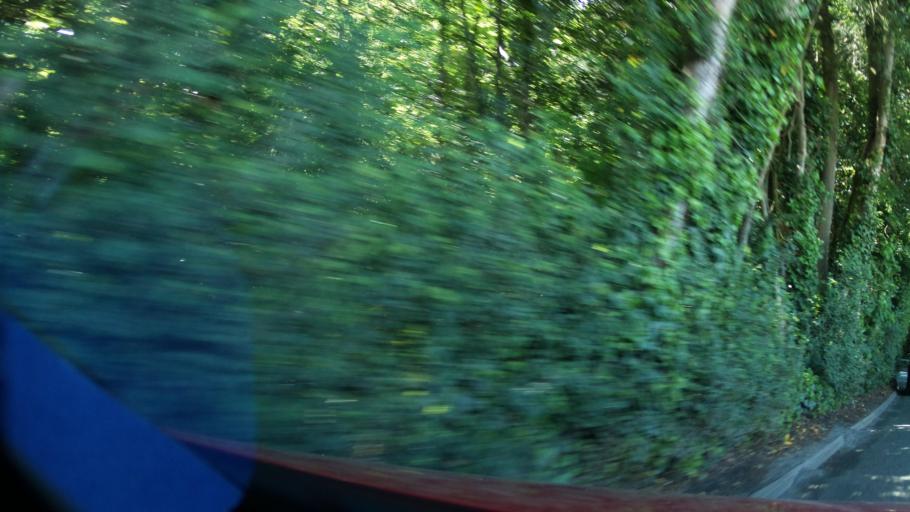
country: GB
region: England
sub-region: Hertfordshire
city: Chorleywood
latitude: 51.6583
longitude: -0.4576
